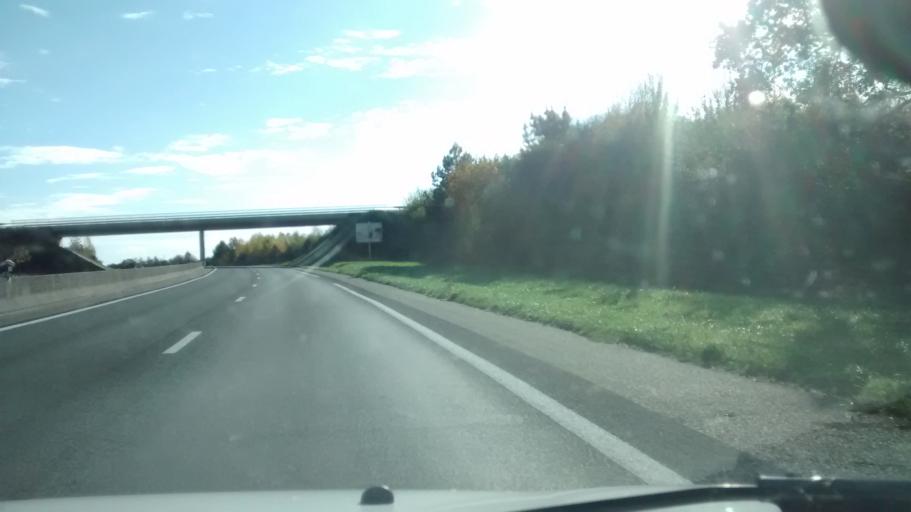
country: FR
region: Pays de la Loire
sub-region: Departement de Maine-et-Loire
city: Pouance
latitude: 47.7387
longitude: -1.1512
